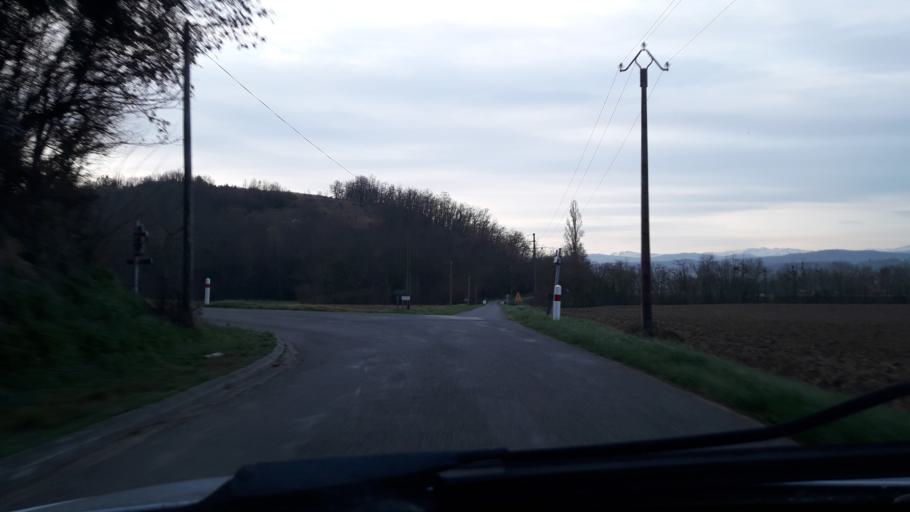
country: FR
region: Midi-Pyrenees
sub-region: Departement de la Haute-Garonne
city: Montesquieu-Volvestre
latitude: 43.1921
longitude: 1.2523
